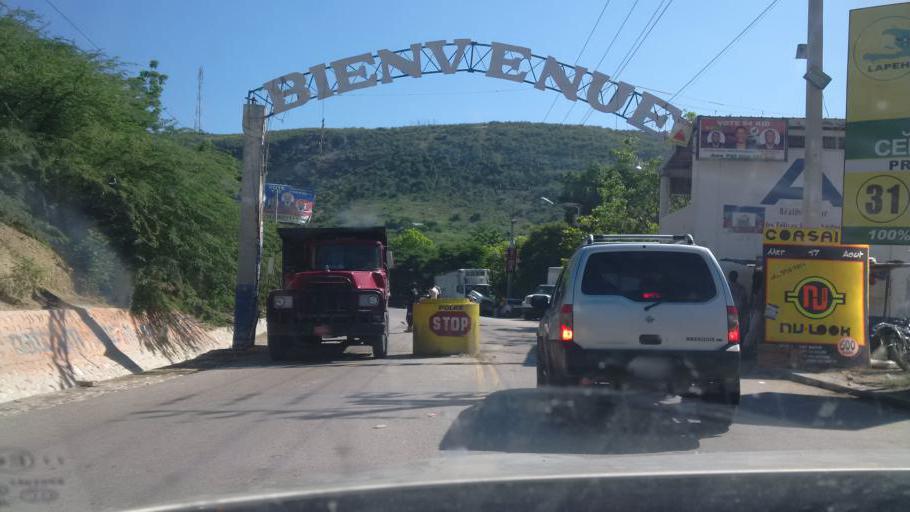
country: HT
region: Artibonite
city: Saint-Marc
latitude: 19.0823
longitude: -72.7197
